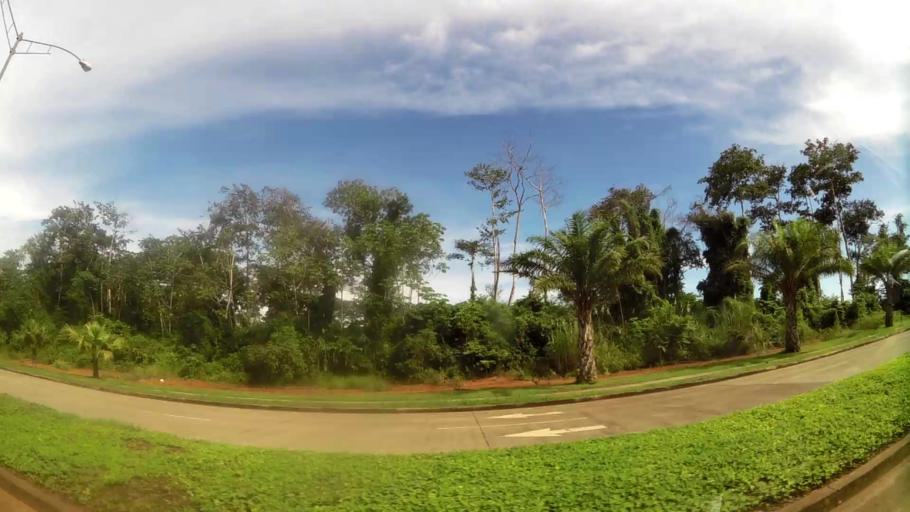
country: PA
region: Panama
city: Puerto Caimito
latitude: 8.8890
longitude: -79.7431
